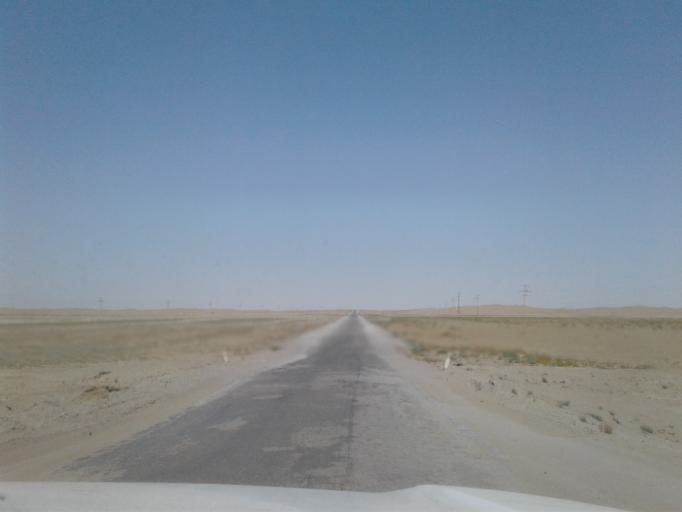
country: TM
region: Balkan
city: Gumdag
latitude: 38.3655
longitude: 54.3840
